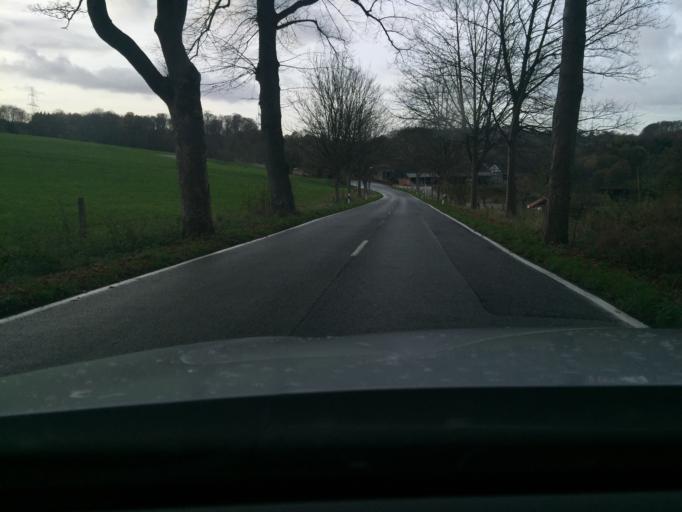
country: DE
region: North Rhine-Westphalia
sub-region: Regierungsbezirk Dusseldorf
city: Velbert
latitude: 51.3735
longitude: 7.0669
